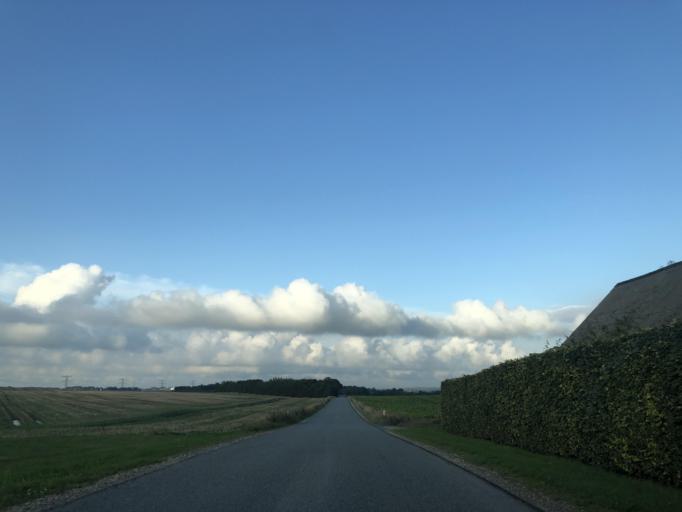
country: DK
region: North Denmark
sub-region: Rebild Kommune
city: Stovring
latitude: 56.9106
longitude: 9.7449
